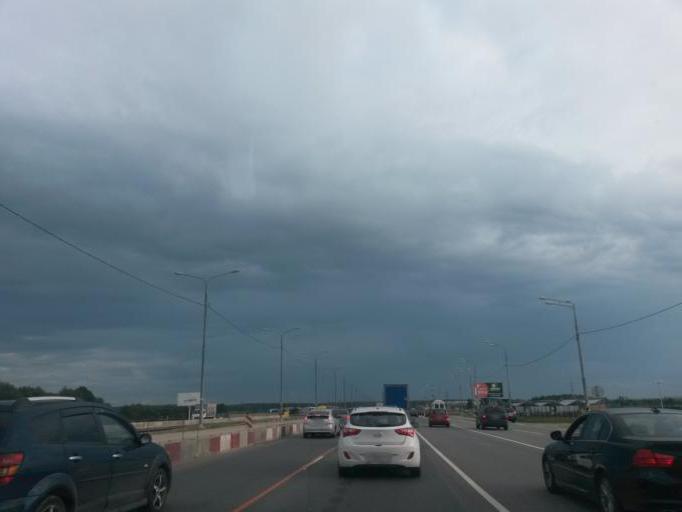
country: RU
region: Moskovskaya
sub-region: Podol'skiy Rayon
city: Podol'sk
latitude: 55.3935
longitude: 37.6047
